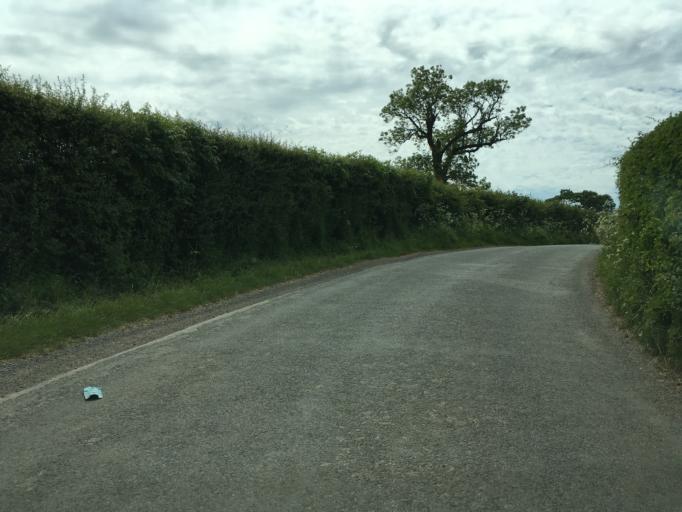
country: GB
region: England
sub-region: South Gloucestershire
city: Charfield
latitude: 51.6625
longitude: -2.4117
